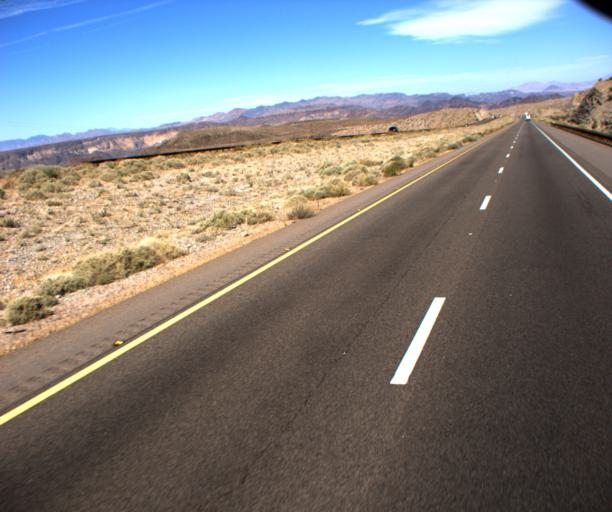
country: US
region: Nevada
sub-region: Clark County
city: Boulder City
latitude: 35.9613
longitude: -114.6645
